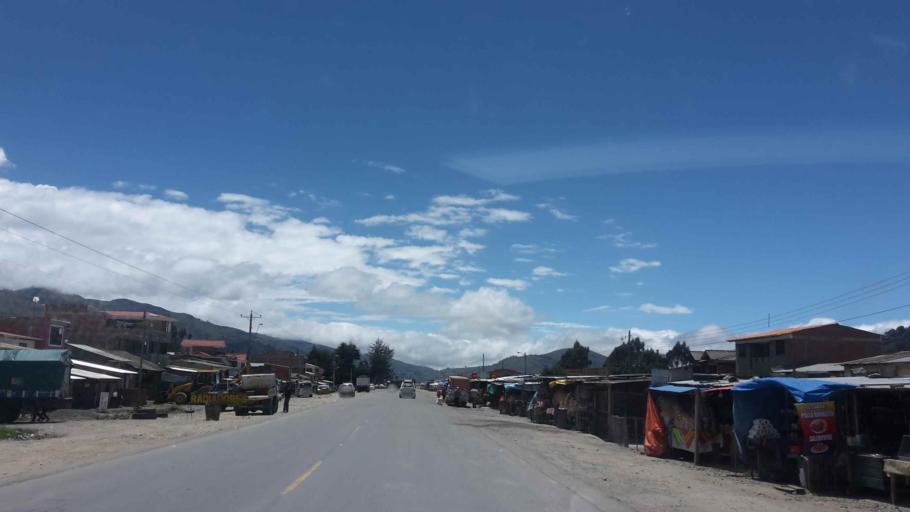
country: BO
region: Cochabamba
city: Colomi
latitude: -17.3327
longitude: -65.8699
